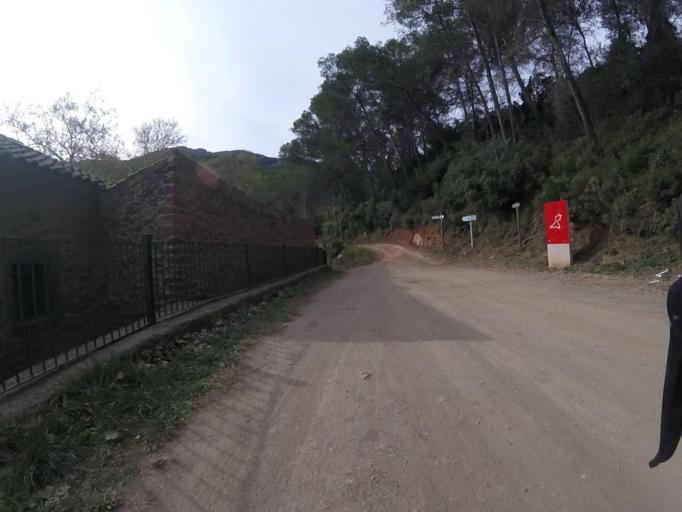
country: ES
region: Valencia
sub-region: Provincia de Castello
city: Cabanes
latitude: 40.1039
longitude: 0.0369
